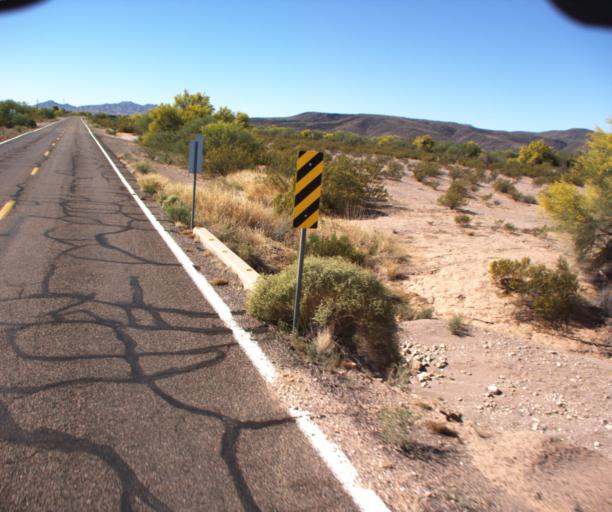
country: US
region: Arizona
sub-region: Pima County
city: Ajo
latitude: 32.5062
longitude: -112.8810
